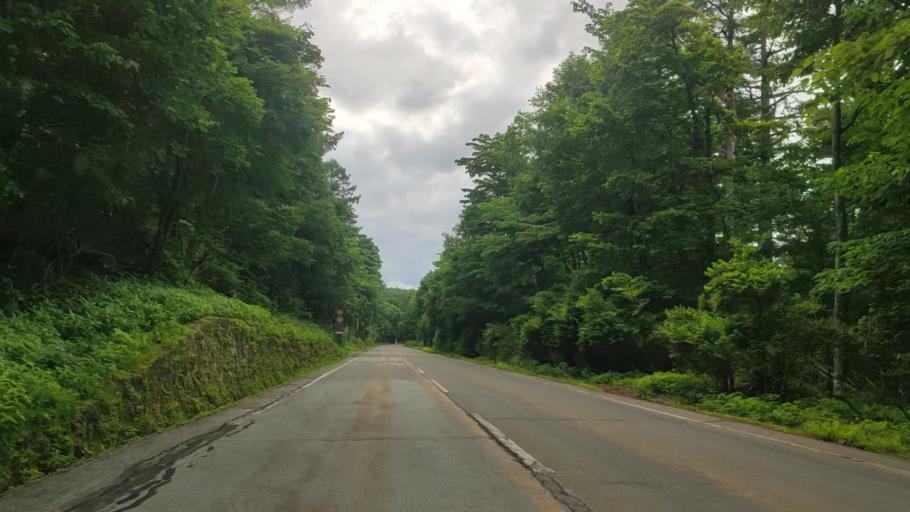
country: JP
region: Yamanashi
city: Fujikawaguchiko
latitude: 35.4222
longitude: 138.7382
